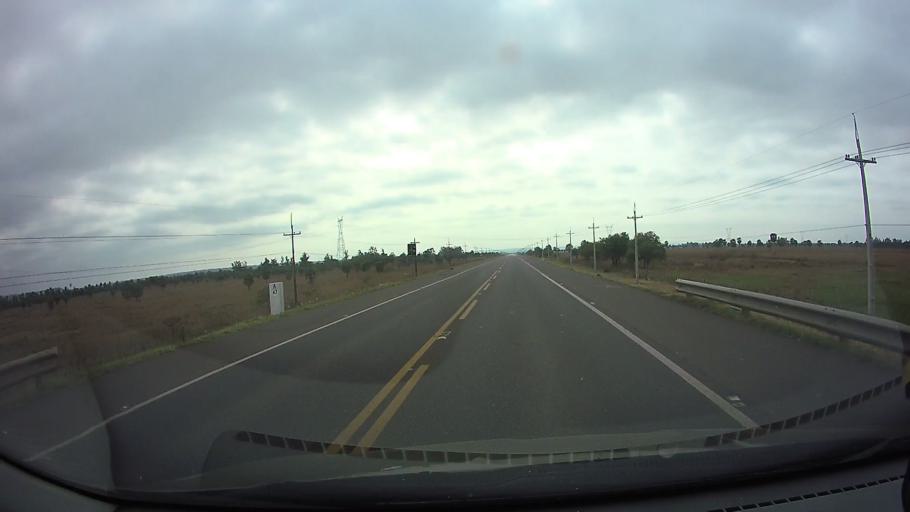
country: PY
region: Cordillera
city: Emboscada
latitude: -25.0876
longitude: -57.2895
